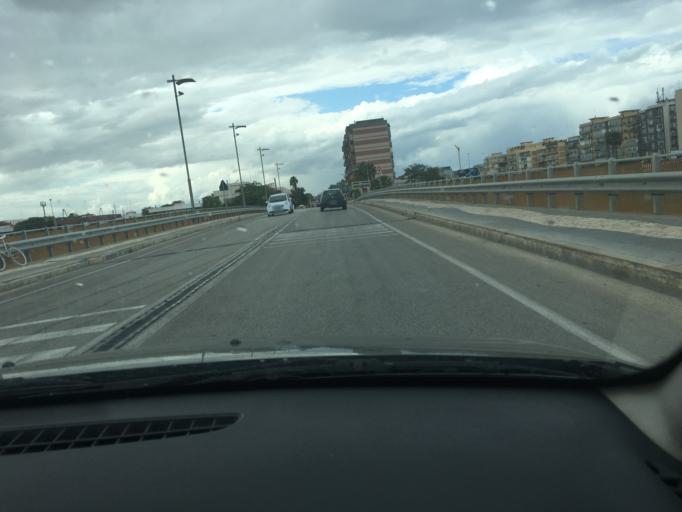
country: IT
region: Apulia
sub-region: Provincia di Bari
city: Bari
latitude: 41.1333
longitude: 16.8285
